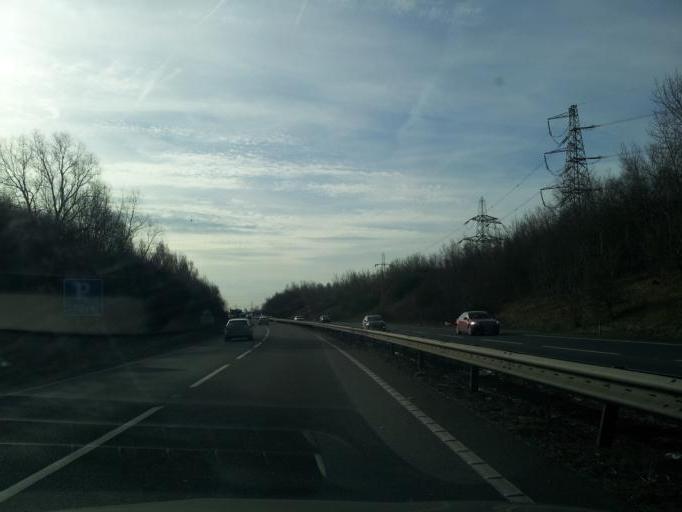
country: GB
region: England
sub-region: Cambridgeshire
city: Eaton Socon
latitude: 52.2171
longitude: -0.2993
